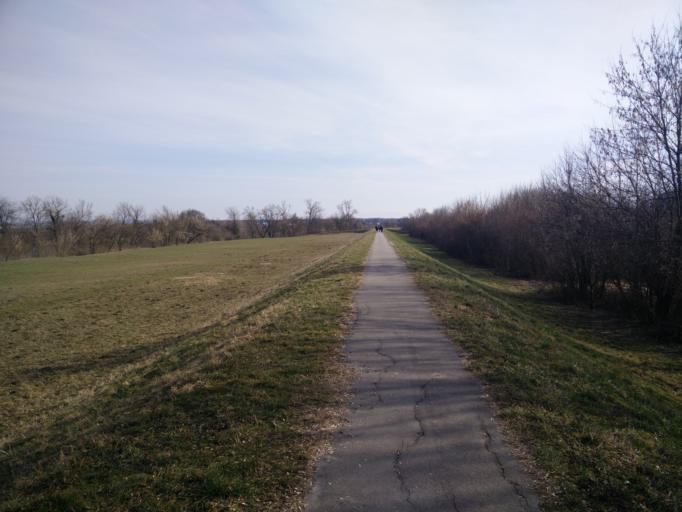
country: HR
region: Karlovacka
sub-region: Grad Karlovac
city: Karlovac
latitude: 45.4958
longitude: 15.5689
